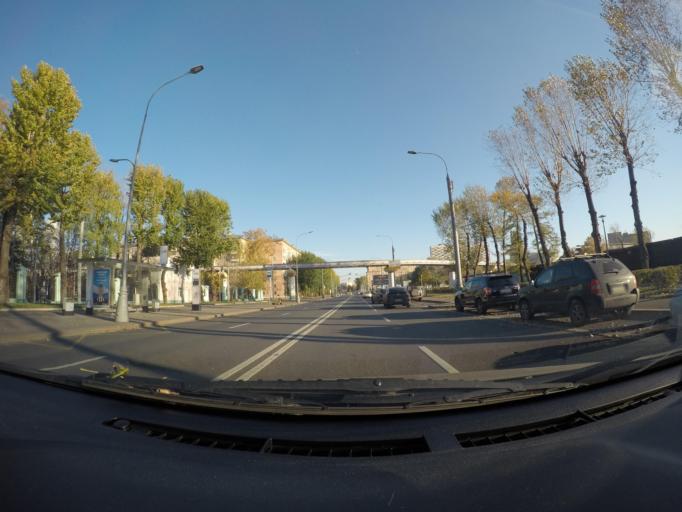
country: RU
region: Moscow
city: Leonovo
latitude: 55.8308
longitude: 37.6444
